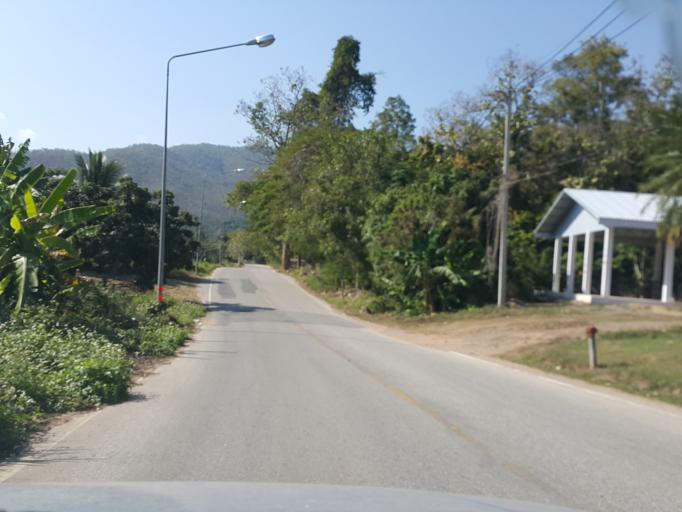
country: TH
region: Chiang Mai
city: Mae Wang
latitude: 18.6187
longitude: 98.7660
